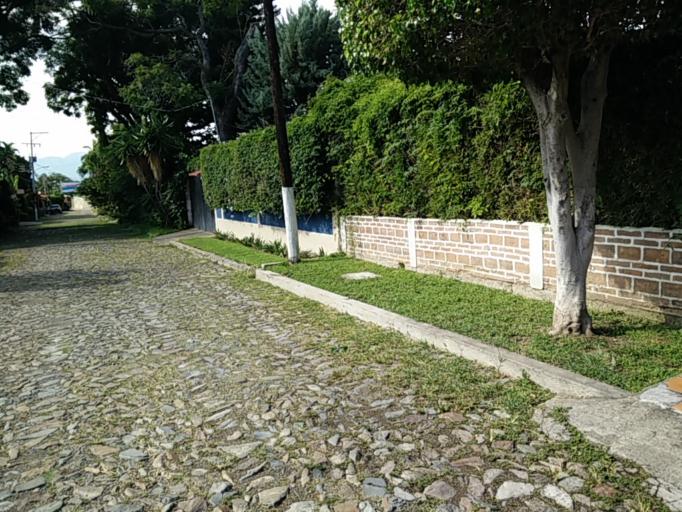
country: MX
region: Jalisco
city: Ajijic
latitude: 20.2991
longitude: -103.2739
